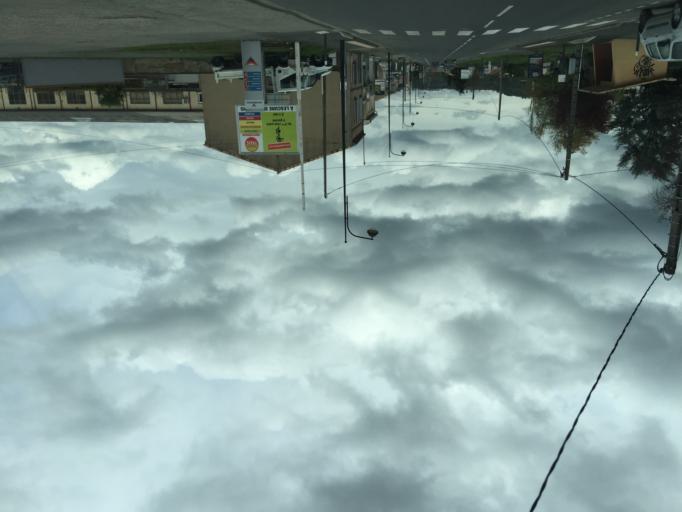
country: FR
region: Midi-Pyrenees
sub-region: Departement du Tarn
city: Albi
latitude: 43.9455
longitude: 2.1512
